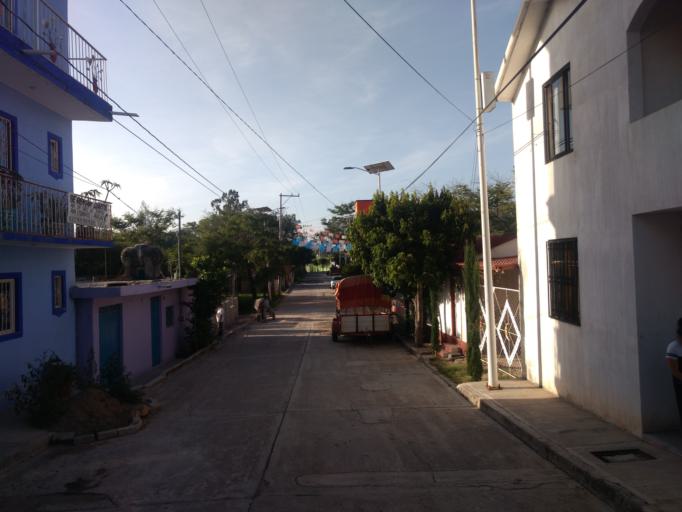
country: MX
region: Oaxaca
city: Ciudad de Huajuapam de Leon
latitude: 17.8171
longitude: -97.7895
